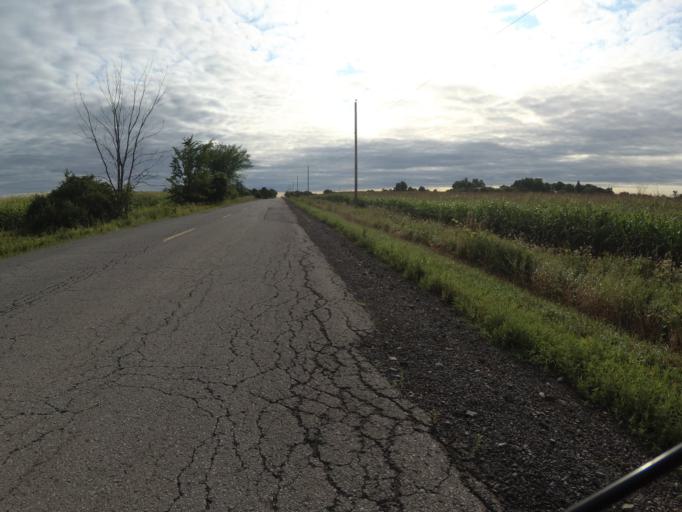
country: CA
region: Ontario
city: Clarence-Rockland
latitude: 45.3211
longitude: -75.3945
